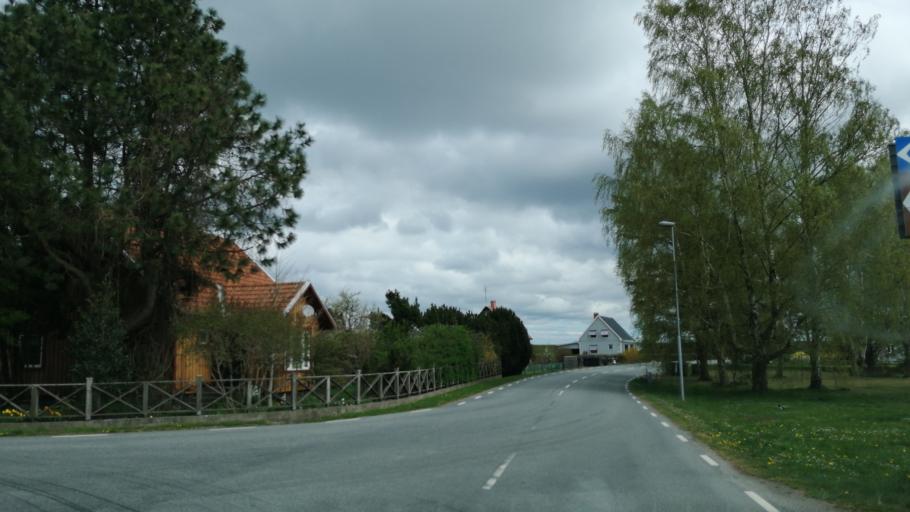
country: SE
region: Skane
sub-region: Kristianstads Kommun
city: Fjalkinge
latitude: 56.0428
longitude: 14.3359
